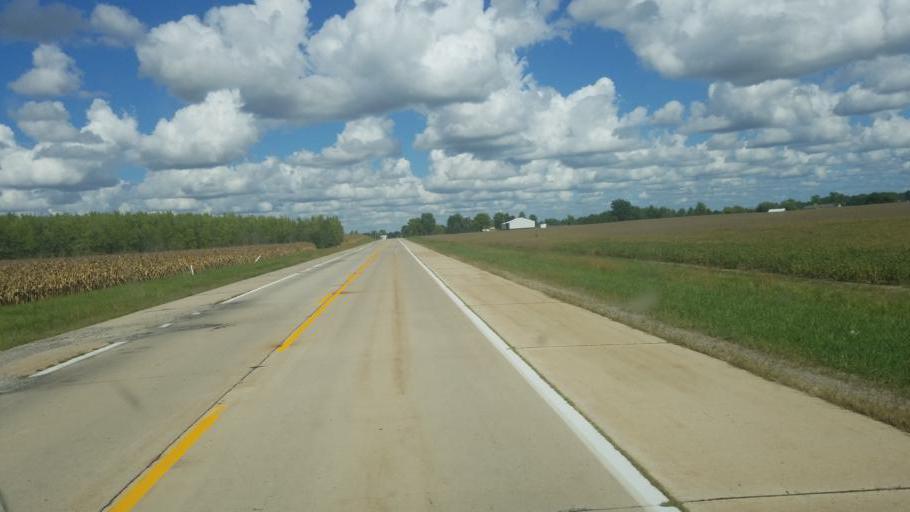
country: US
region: Ohio
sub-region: Champaign County
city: North Lewisburg
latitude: 40.3232
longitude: -83.4845
